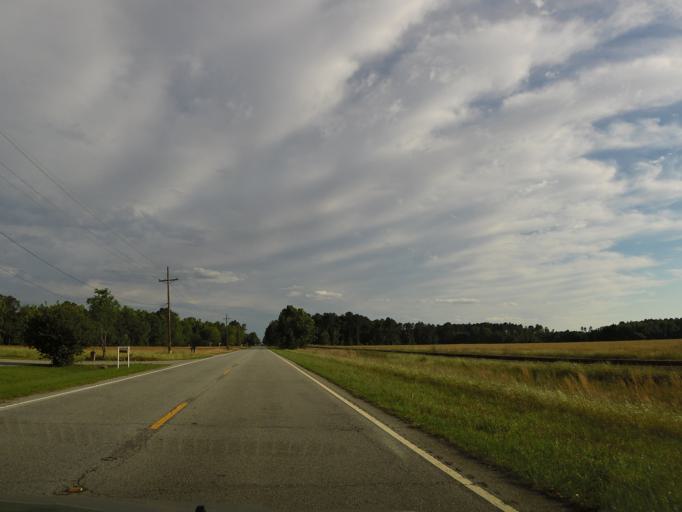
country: US
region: South Carolina
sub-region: Hampton County
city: Estill
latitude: 32.6941
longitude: -81.2428
